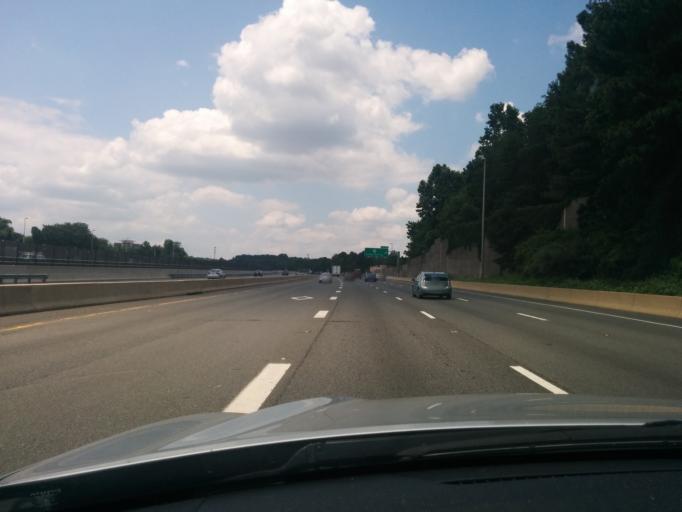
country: US
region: Virginia
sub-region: Fairfax County
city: Wolf Trap
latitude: 38.9483
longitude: -77.3025
